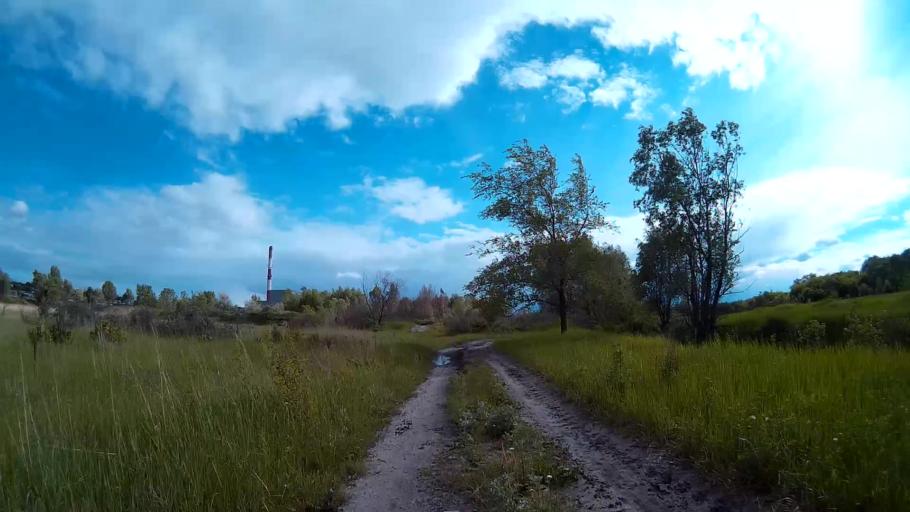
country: RU
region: Ulyanovsk
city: Novoul'yanovsk
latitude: 54.2334
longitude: 48.2846
